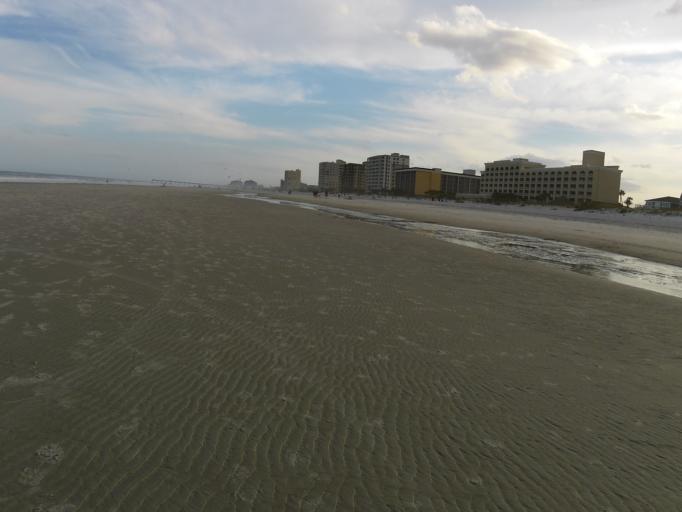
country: US
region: Florida
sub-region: Duval County
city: Neptune Beach
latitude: 30.3058
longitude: -81.3908
